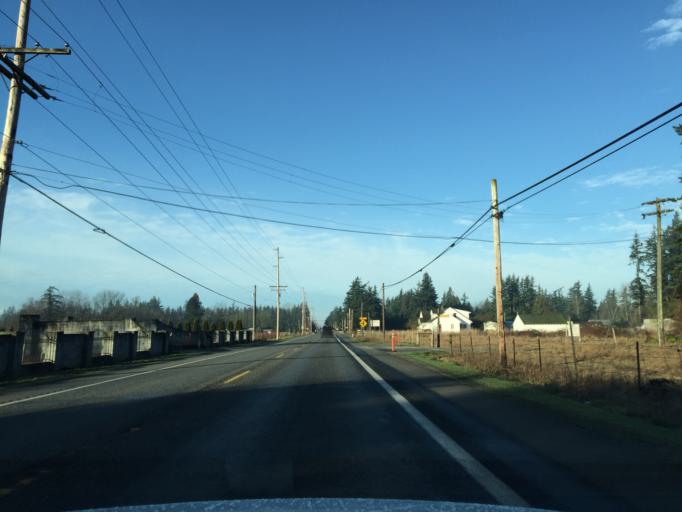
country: US
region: Washington
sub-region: Whatcom County
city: Lynden
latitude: 48.9353
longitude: -122.5255
